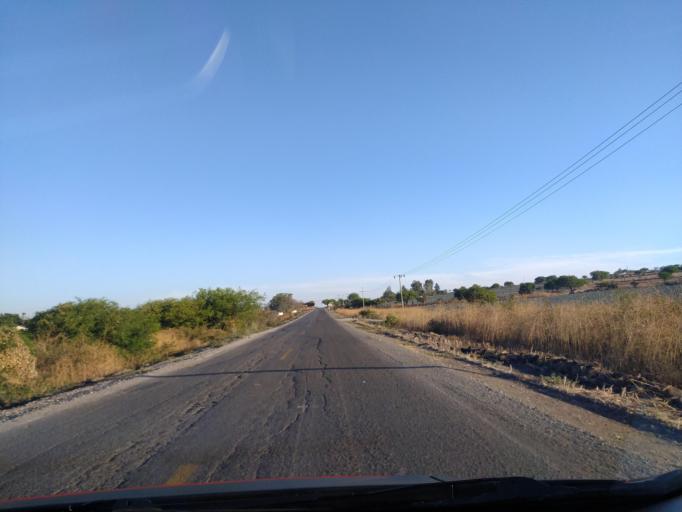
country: MX
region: Guanajuato
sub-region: San Francisco del Rincon
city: San Ignacio de Hidalgo
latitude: 20.8179
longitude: -101.8405
